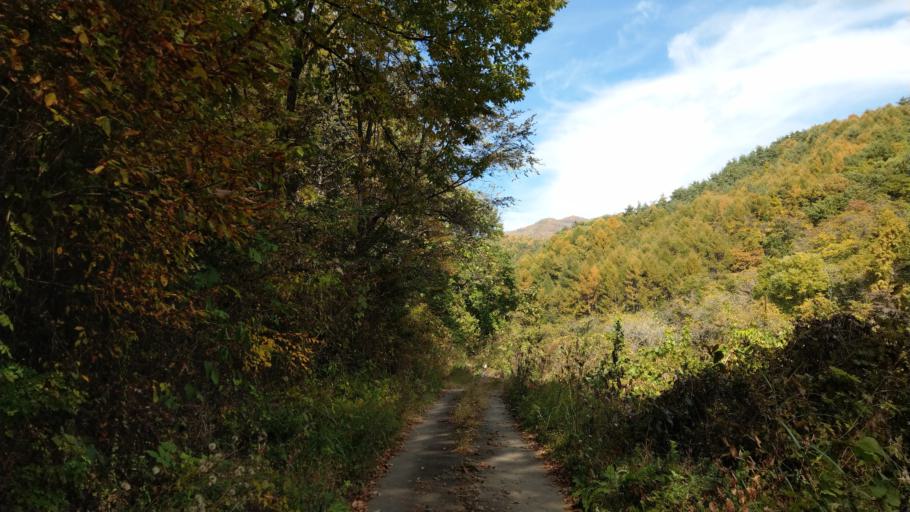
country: JP
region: Nagano
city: Komoro
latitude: 36.3666
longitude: 138.4410
